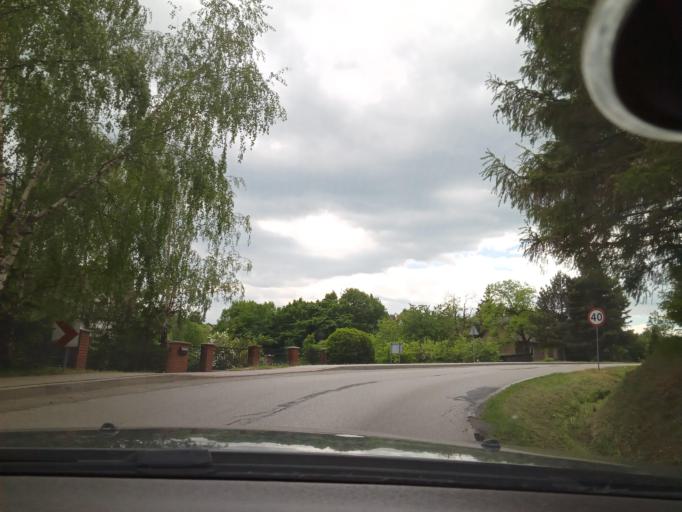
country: PL
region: Lesser Poland Voivodeship
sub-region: Powiat bochenski
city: Lapanow
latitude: 49.8106
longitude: 20.3186
